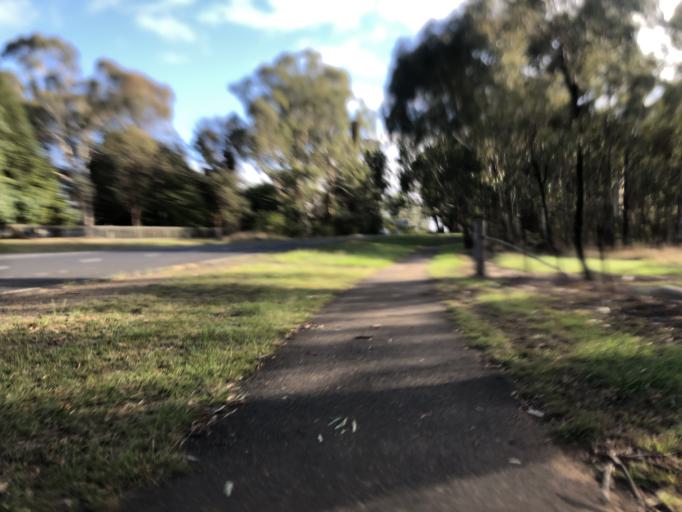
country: AU
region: New South Wales
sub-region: Orange Municipality
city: Orange
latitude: -33.3220
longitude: 149.0867
